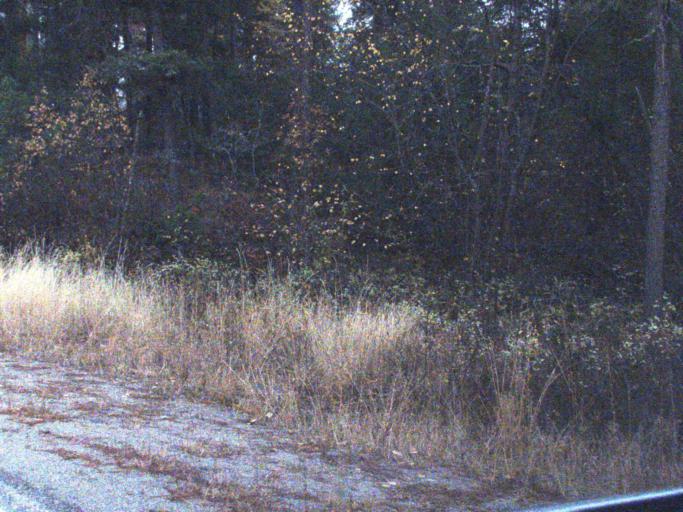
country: CA
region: British Columbia
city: Grand Forks
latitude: 48.9106
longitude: -118.2053
